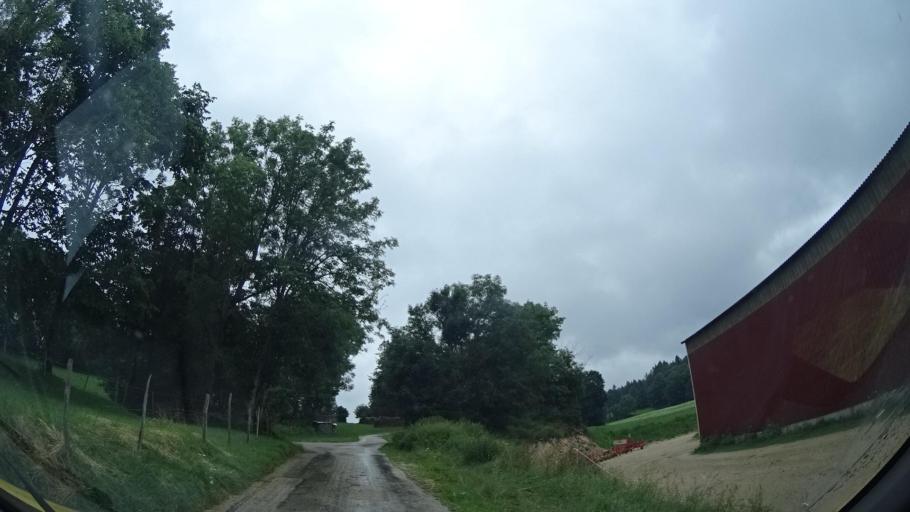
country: FR
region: Franche-Comte
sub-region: Departement du Doubs
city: Les Fourgs
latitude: 46.8257
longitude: 6.3452
